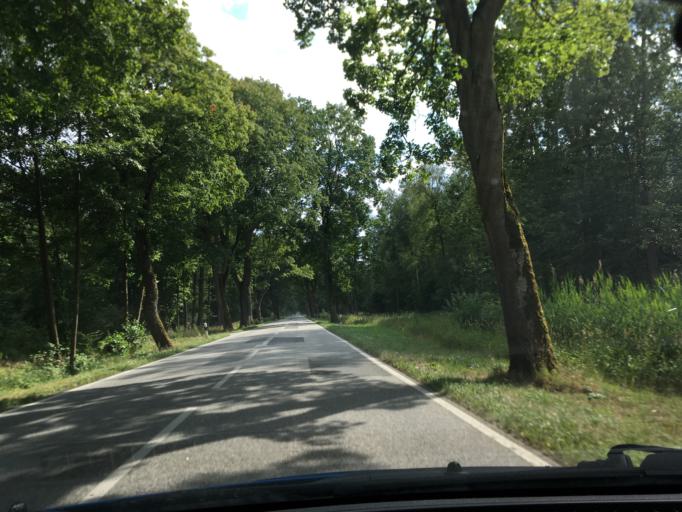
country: DE
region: Mecklenburg-Vorpommern
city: Lubtheen
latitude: 53.3512
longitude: 11.0862
